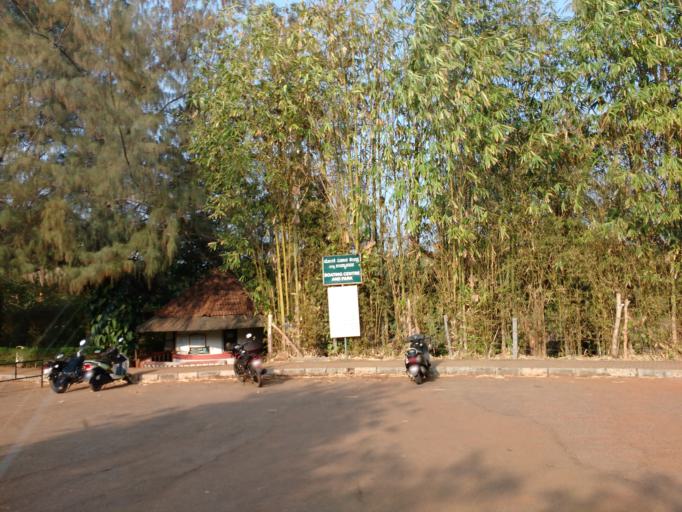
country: IN
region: Karnataka
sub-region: Dakshina Kannada
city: Mangalore
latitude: 12.9286
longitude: 74.8948
